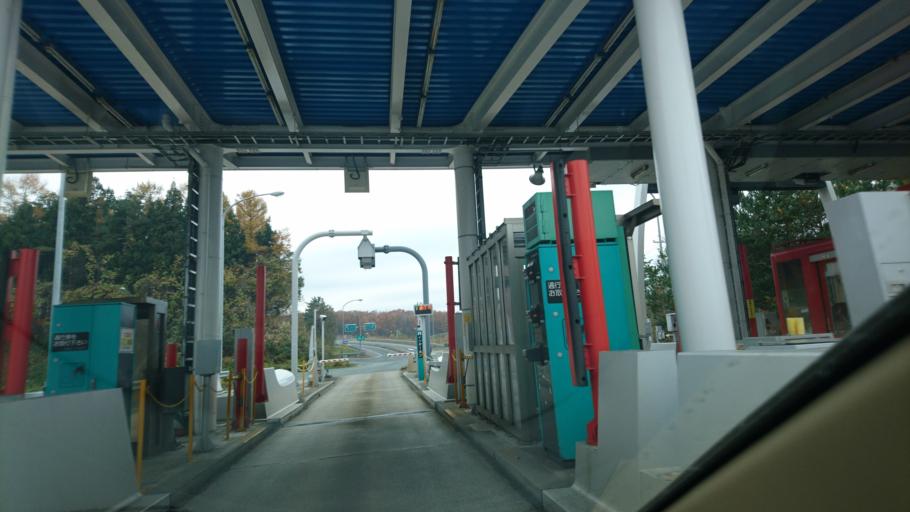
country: JP
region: Iwate
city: Kitakami
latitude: 39.2393
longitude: 141.0819
